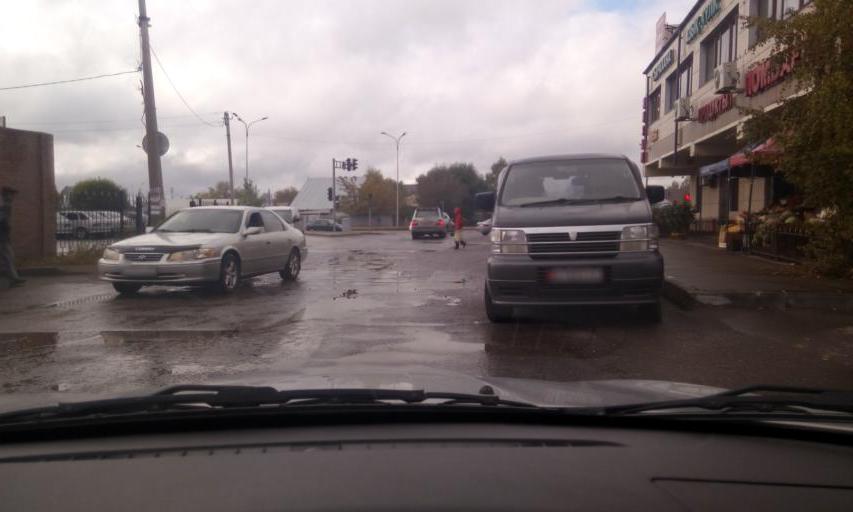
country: KZ
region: Astana Qalasy
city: Astana
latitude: 51.1827
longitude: 71.3769
